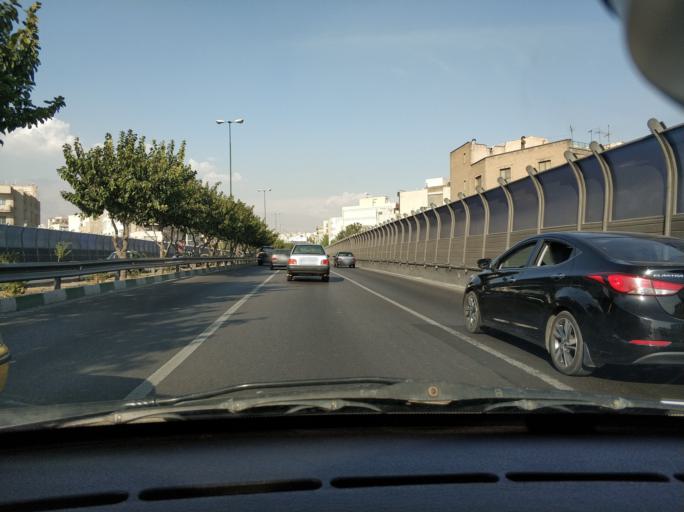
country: IR
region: Tehran
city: Tehran
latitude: 35.7207
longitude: 51.3603
